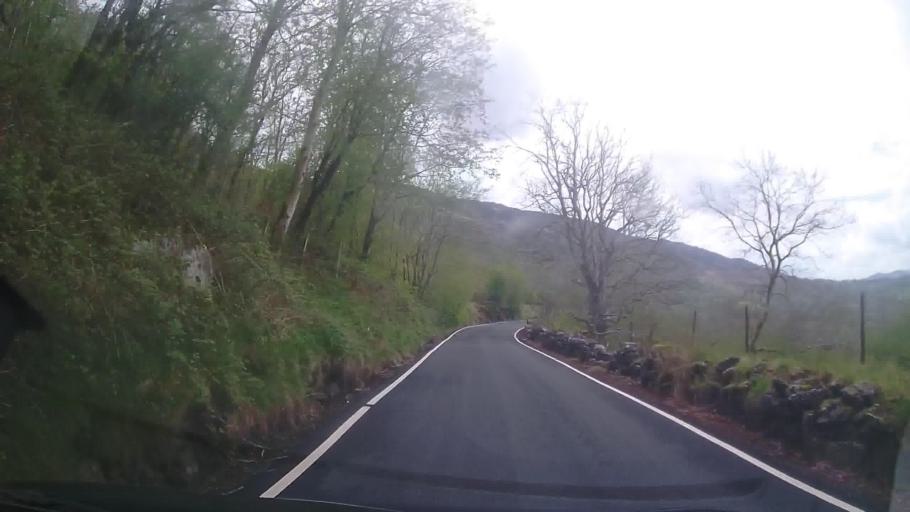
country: GB
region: Wales
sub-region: Gwynedd
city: Blaenau-Ffestiniog
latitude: 53.0590
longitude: -4.0036
